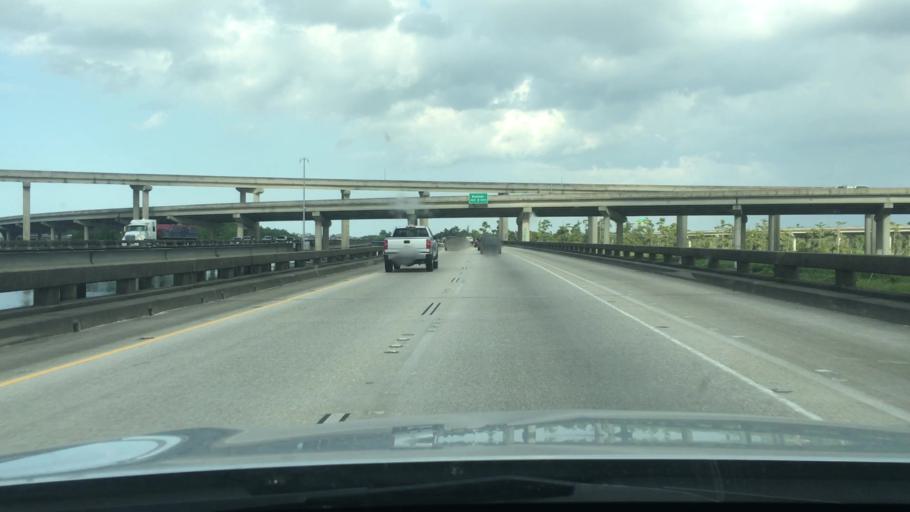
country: US
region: Louisiana
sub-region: Jefferson Parish
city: Kenner
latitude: 30.0068
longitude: -90.2942
